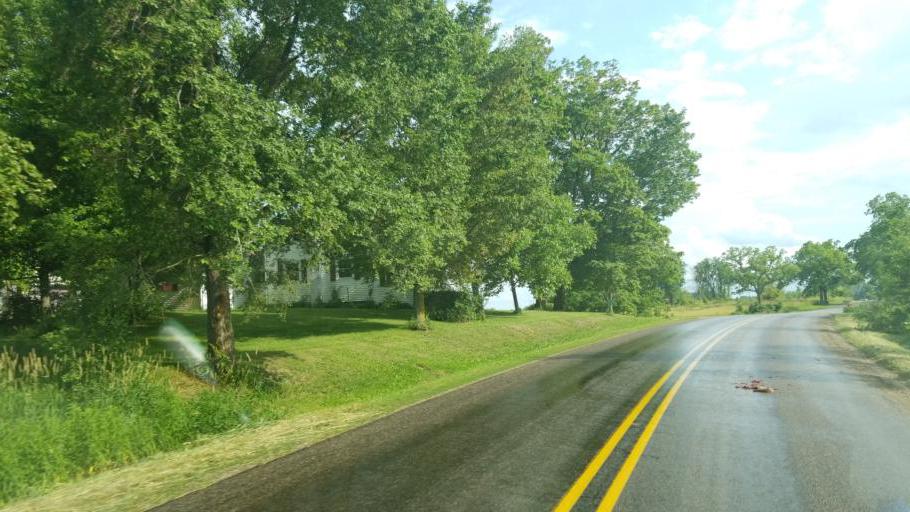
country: US
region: Michigan
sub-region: Eaton County
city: Bellevue
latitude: 42.5123
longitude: -85.0136
